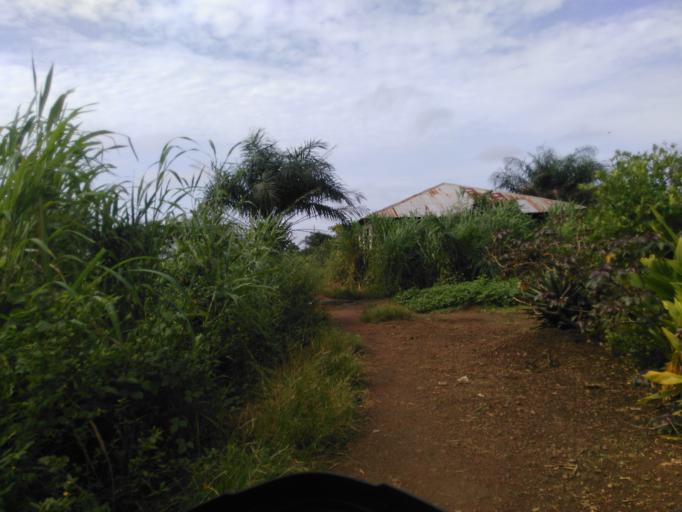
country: SL
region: Southern Province
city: Rotifunk
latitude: 8.4815
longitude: -12.7568
